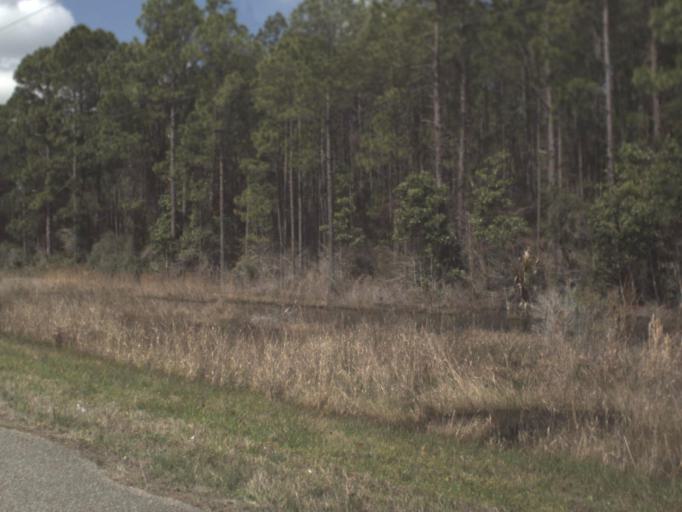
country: US
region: Florida
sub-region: Franklin County
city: Apalachicola
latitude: 29.7225
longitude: -85.0993
